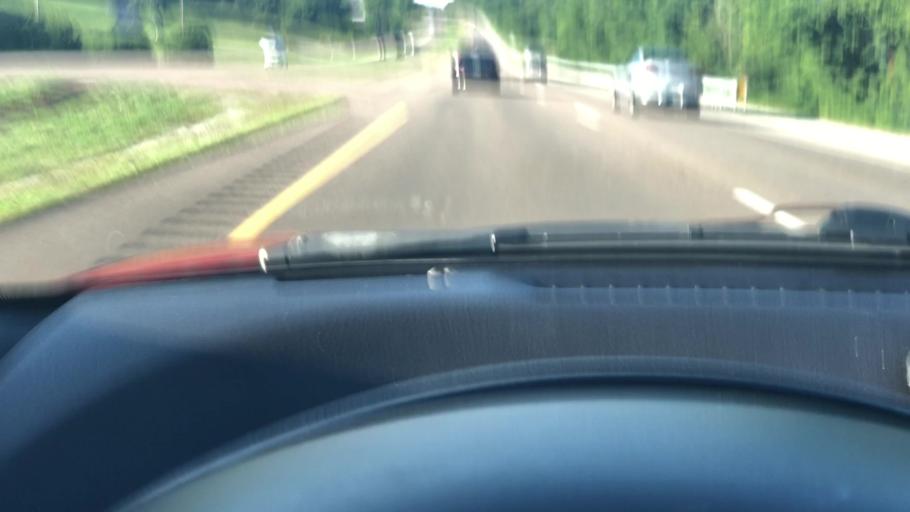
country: US
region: Tennessee
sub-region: Jefferson County
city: Jefferson City
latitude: 36.0708
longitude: -83.4770
